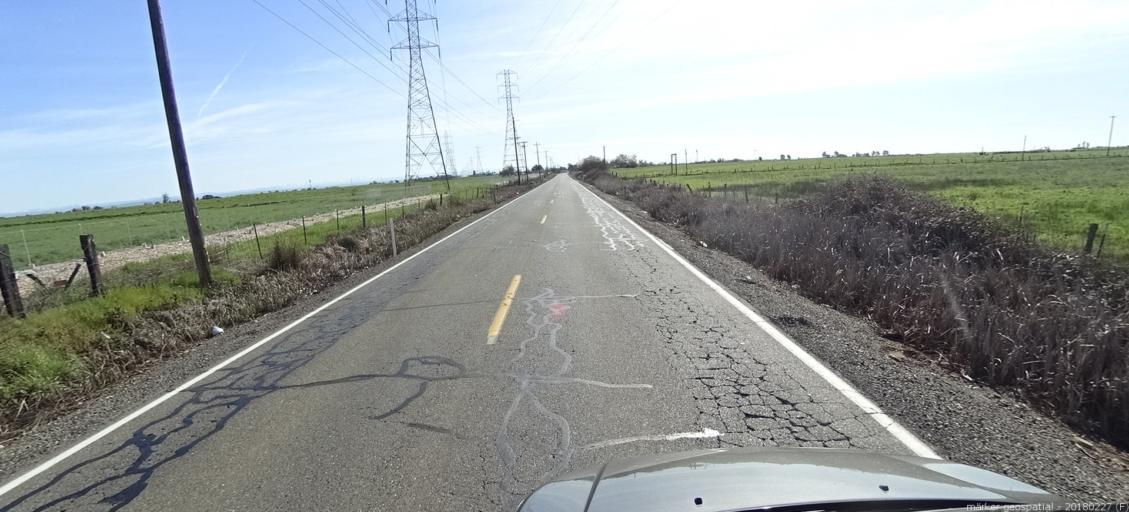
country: US
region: California
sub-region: Sacramento County
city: Vineyard
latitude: 38.5108
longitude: -121.3221
